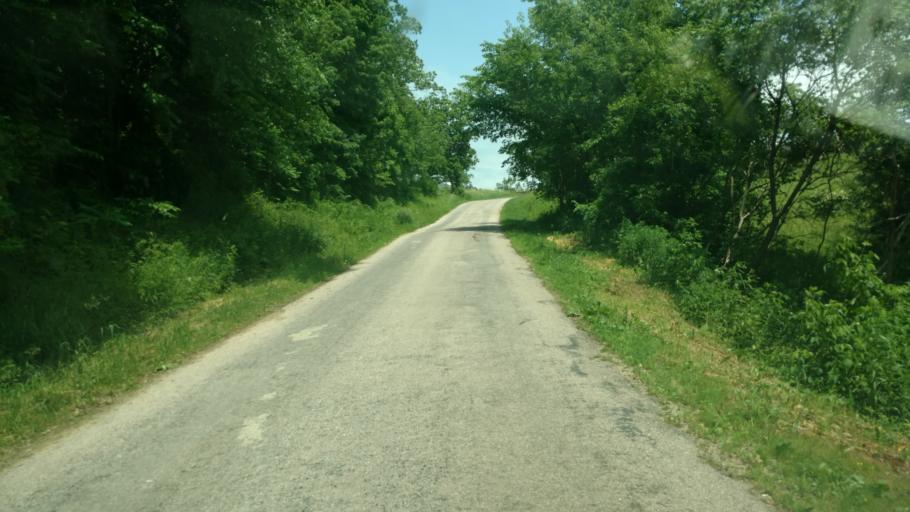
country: US
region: Wisconsin
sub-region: Monroe County
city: Cashton
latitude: 43.6867
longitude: -90.6800
